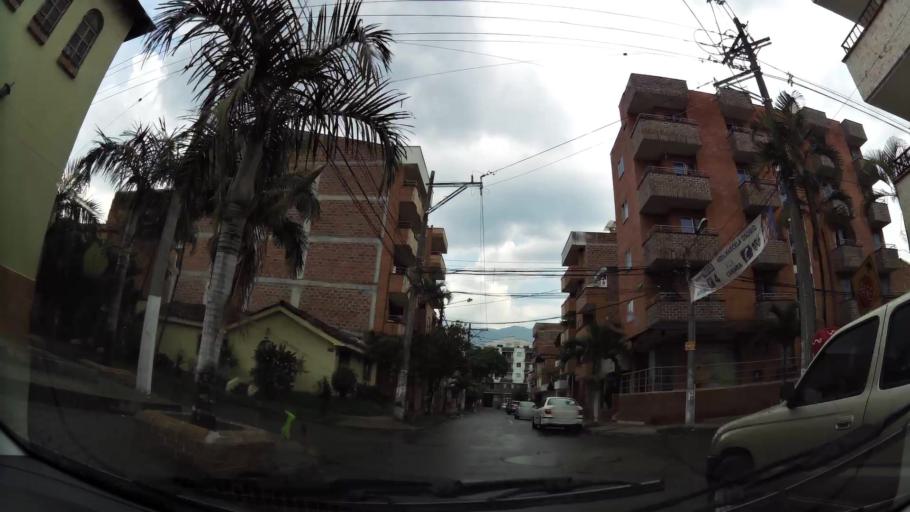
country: CO
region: Antioquia
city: Itagui
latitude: 6.1838
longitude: -75.5941
